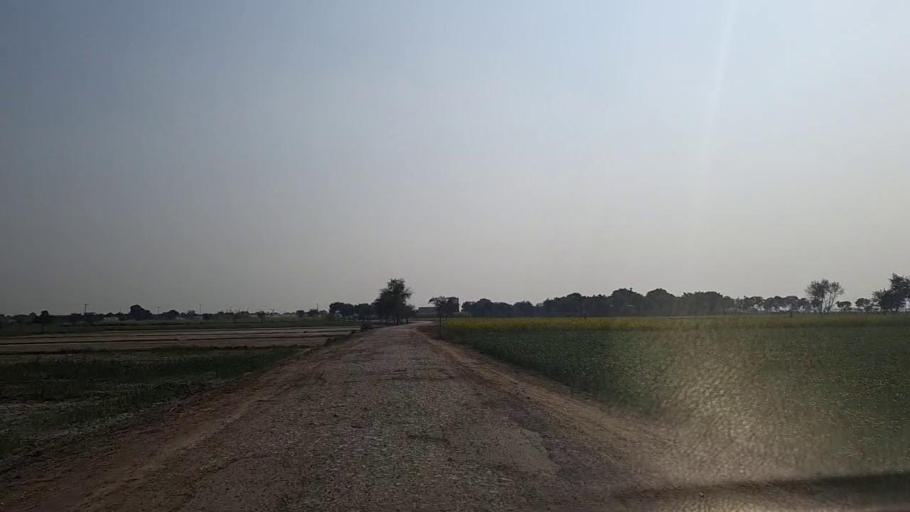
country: PK
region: Sindh
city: Daur
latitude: 26.4024
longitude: 68.4176
